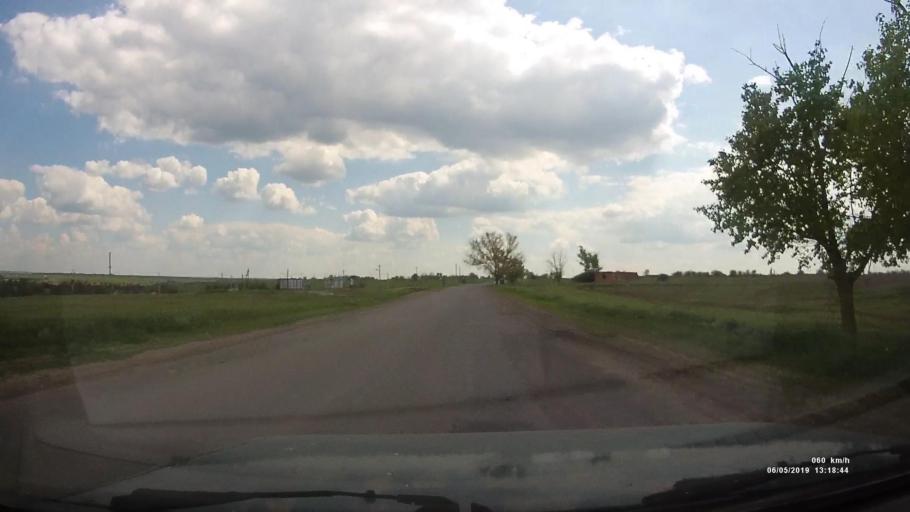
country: RU
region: Rostov
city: Ust'-Donetskiy
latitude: 47.7315
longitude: 40.9134
